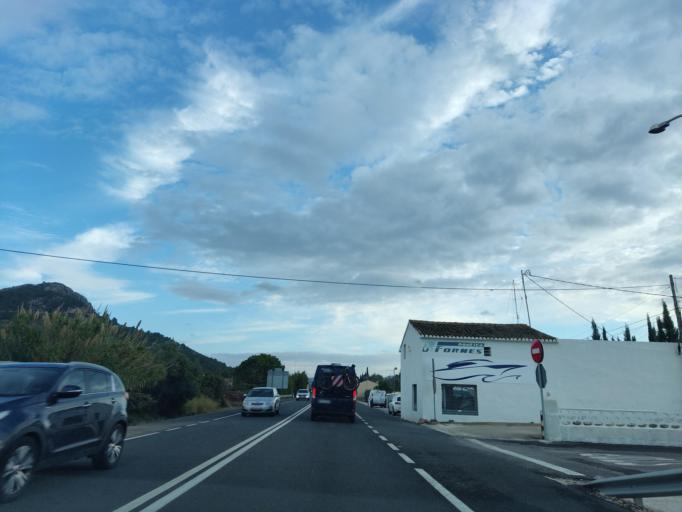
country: ES
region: Valencia
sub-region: Provincia de Alicante
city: Pedreguer
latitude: 38.8129
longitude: 0.0306
